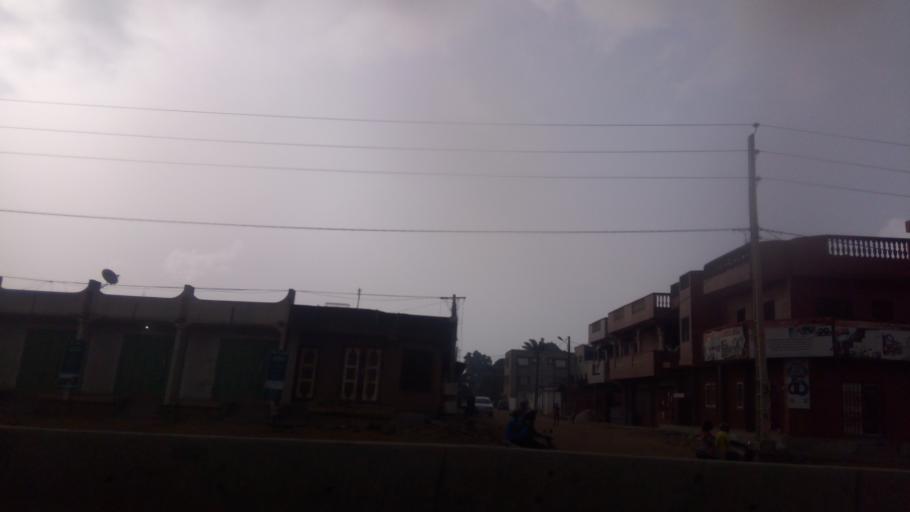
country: BJ
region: Atlantique
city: Abomey-Calavi
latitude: 6.3838
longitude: 2.3457
